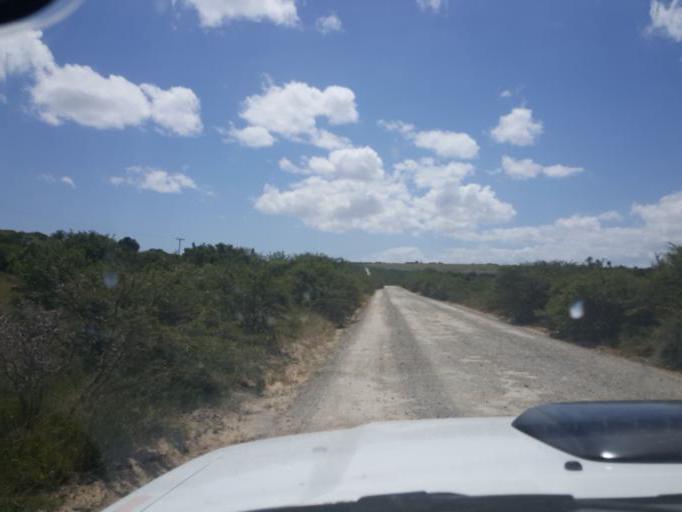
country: ZA
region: Eastern Cape
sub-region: Cacadu District Municipality
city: Grahamstown
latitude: -33.5467
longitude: 26.1117
